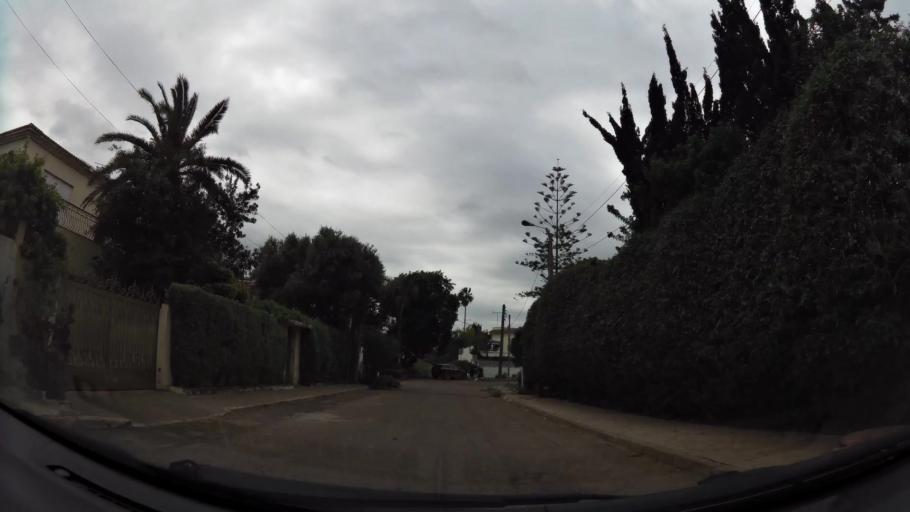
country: MA
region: Grand Casablanca
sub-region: Casablanca
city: Casablanca
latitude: 33.5521
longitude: -7.6358
